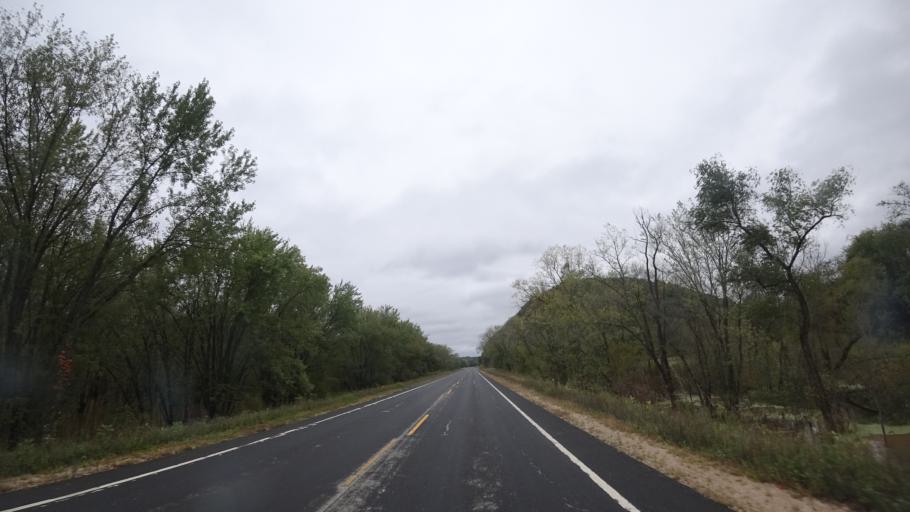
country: US
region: Wisconsin
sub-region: Grant County
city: Boscobel
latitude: 43.1866
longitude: -90.6707
